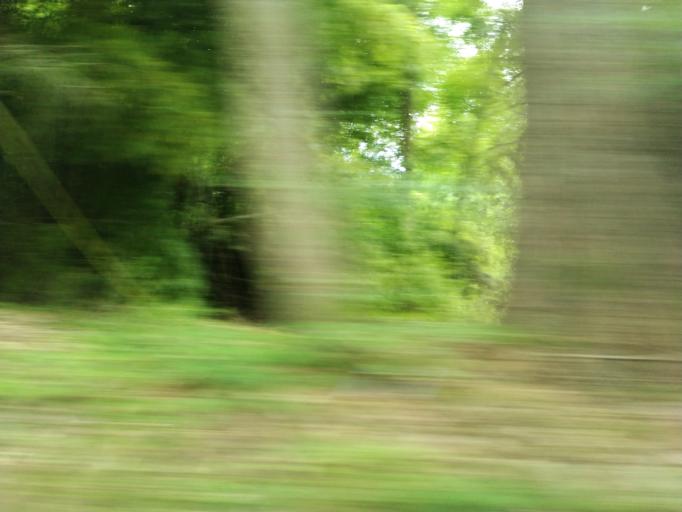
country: US
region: Maryland
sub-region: Anne Arundel County
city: Deale
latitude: 38.8233
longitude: -76.5820
